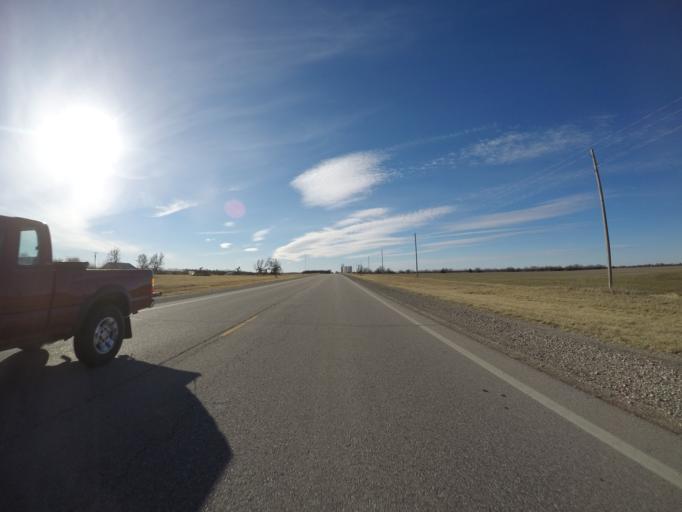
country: US
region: Kansas
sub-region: McPherson County
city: Moundridge
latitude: 38.3768
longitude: -97.4463
